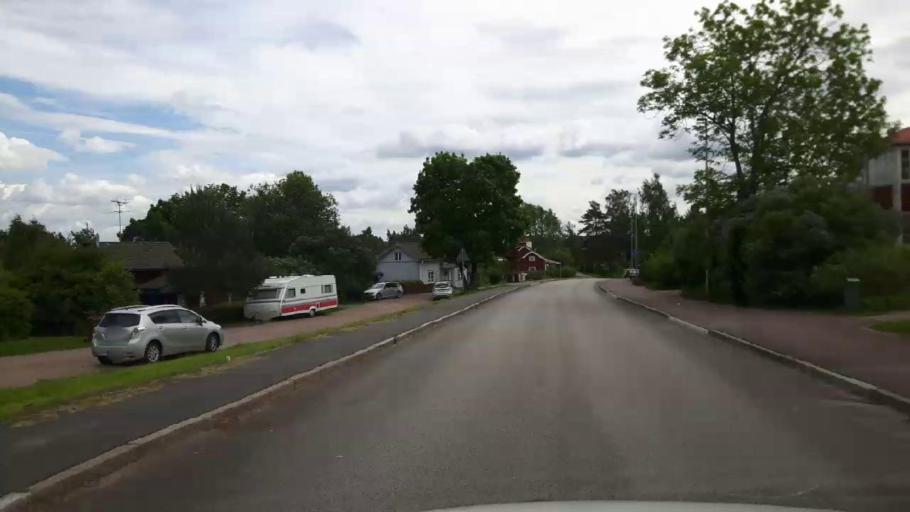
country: SE
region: Dalarna
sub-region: Hedemora Kommun
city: Hedemora
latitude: 60.2697
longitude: 15.9967
